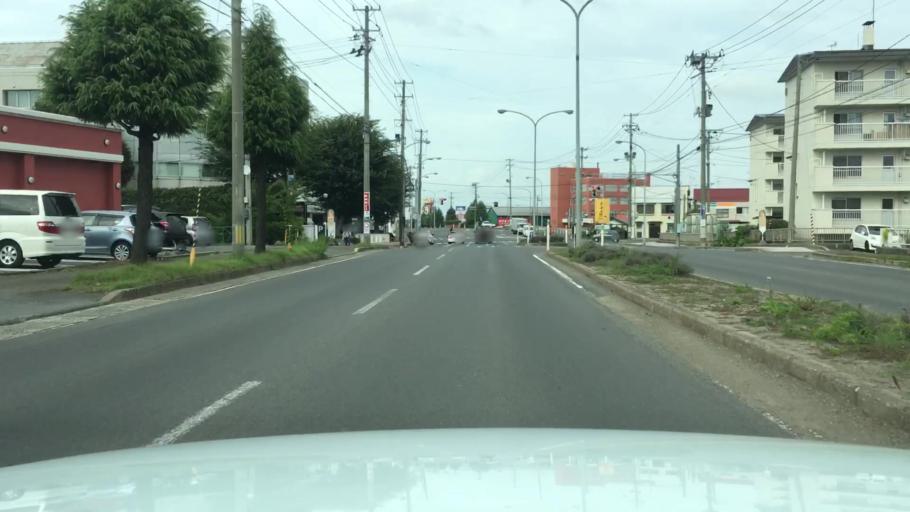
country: JP
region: Aomori
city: Hirosaki
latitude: 40.6090
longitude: 140.4806
